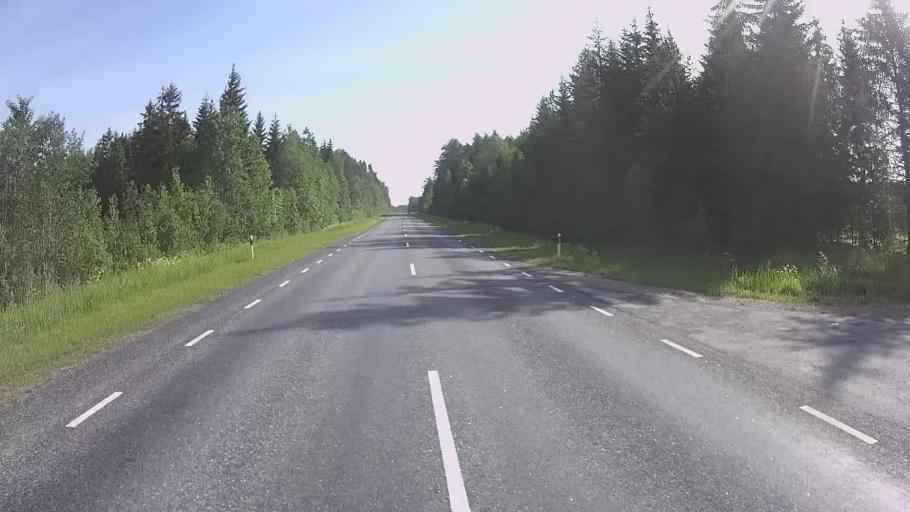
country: EE
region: Valgamaa
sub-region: Torva linn
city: Torva
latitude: 58.0492
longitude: 25.9902
